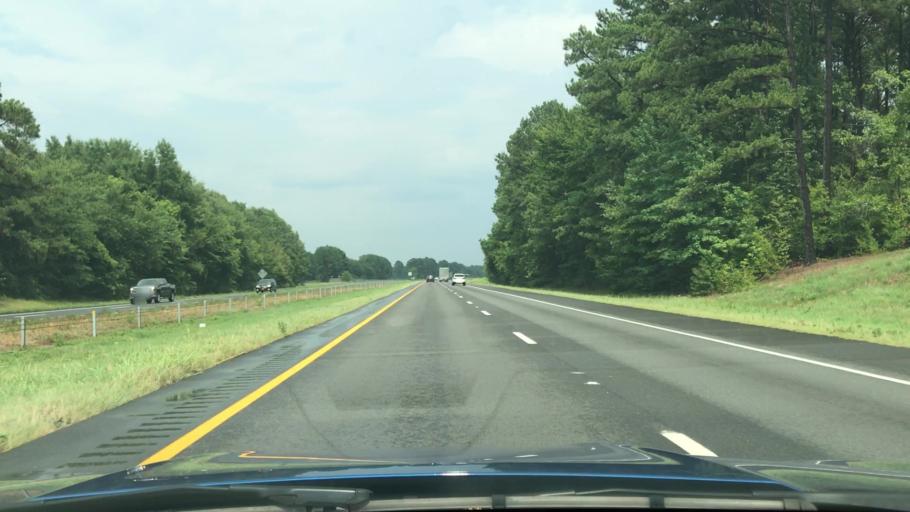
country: US
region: Texas
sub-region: Harrison County
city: Hallsville
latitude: 32.4831
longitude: -94.5301
